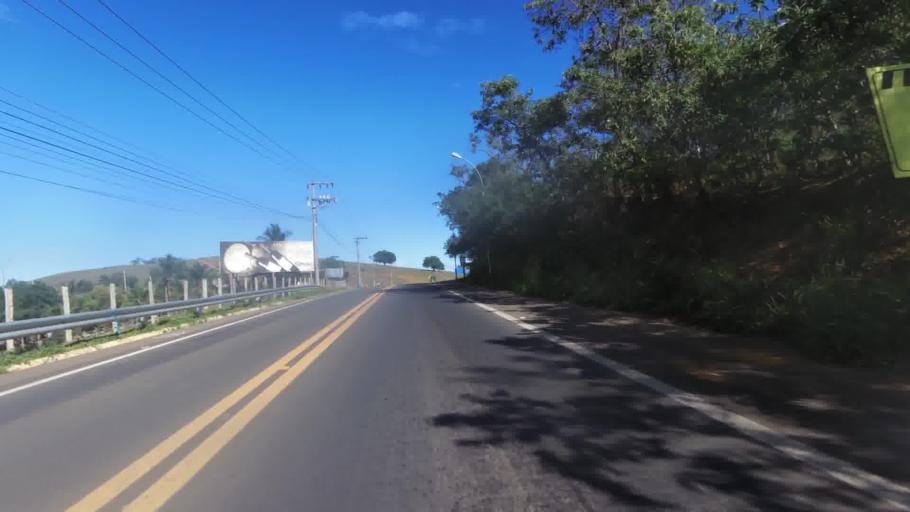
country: BR
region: Espirito Santo
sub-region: Piuma
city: Piuma
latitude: -20.8062
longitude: -40.6678
